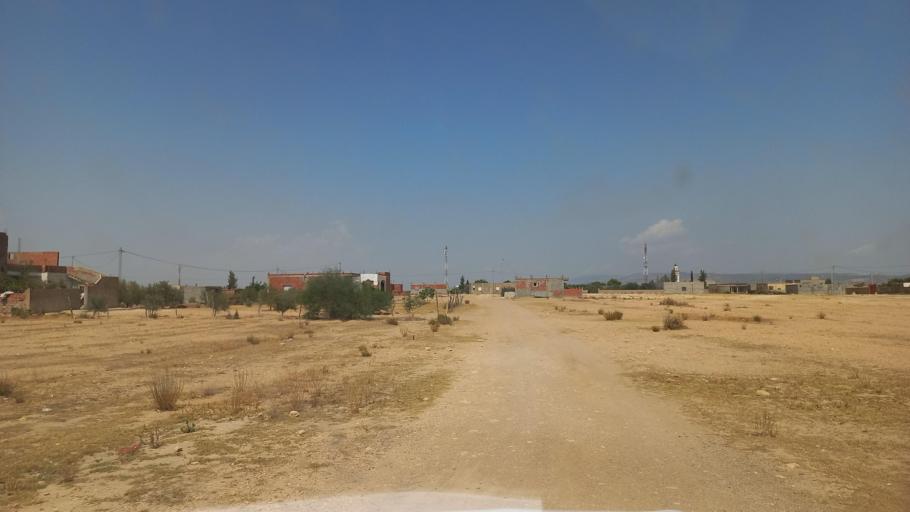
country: TN
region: Al Qasrayn
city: Kasserine
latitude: 35.2492
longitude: 9.0213
